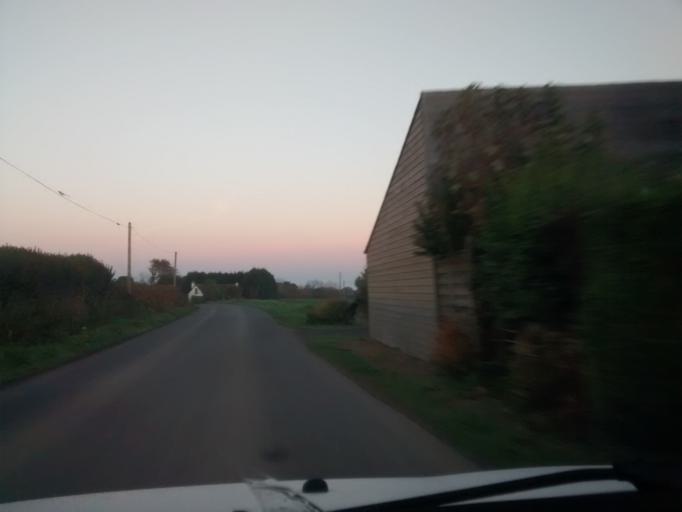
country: FR
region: Brittany
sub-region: Departement des Cotes-d'Armor
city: Trevou-Treguignec
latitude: 48.7882
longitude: -3.3341
